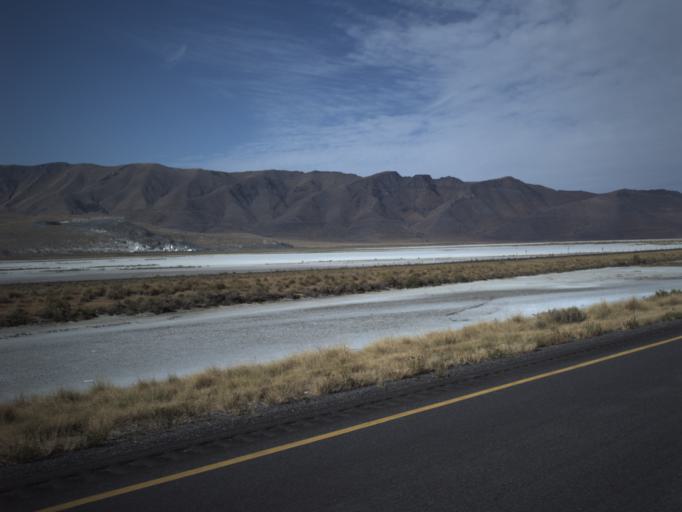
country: US
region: Utah
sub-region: Tooele County
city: Grantsville
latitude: 40.7116
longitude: -112.5337
